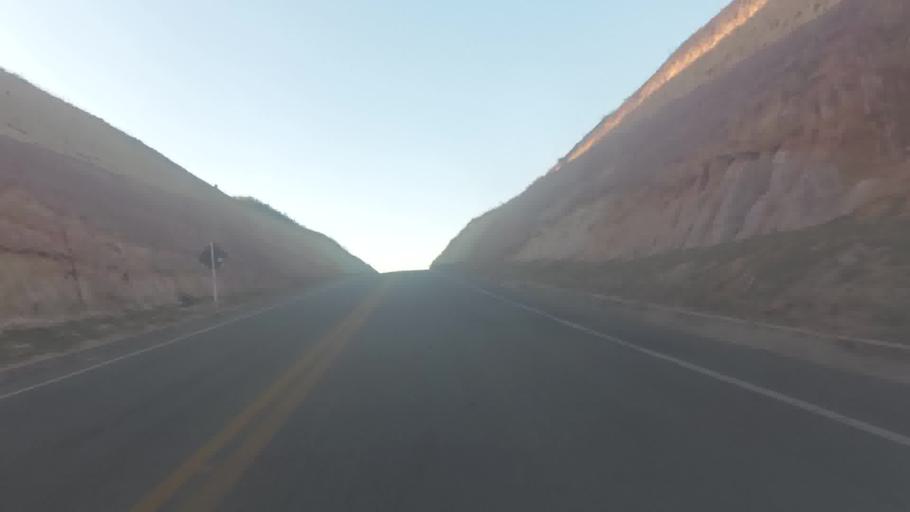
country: BR
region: Espirito Santo
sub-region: Marataizes
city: Marataizes
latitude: -21.1728
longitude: -40.9179
